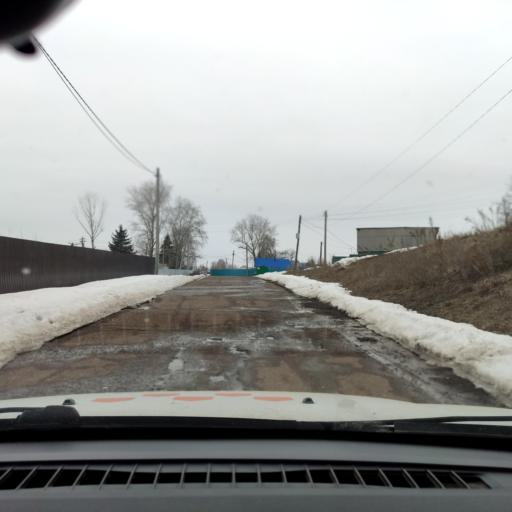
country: RU
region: Bashkortostan
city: Kushnarenkovo
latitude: 55.1189
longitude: 55.3539
